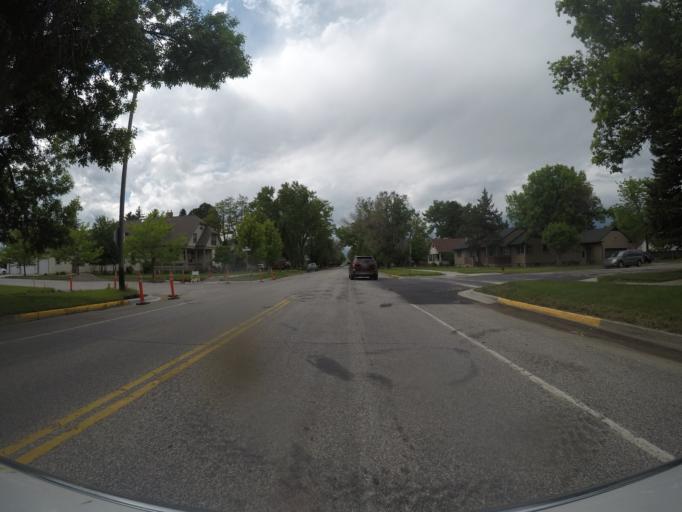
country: US
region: Montana
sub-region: Sweet Grass County
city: Big Timber
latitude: 45.8301
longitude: -109.9494
